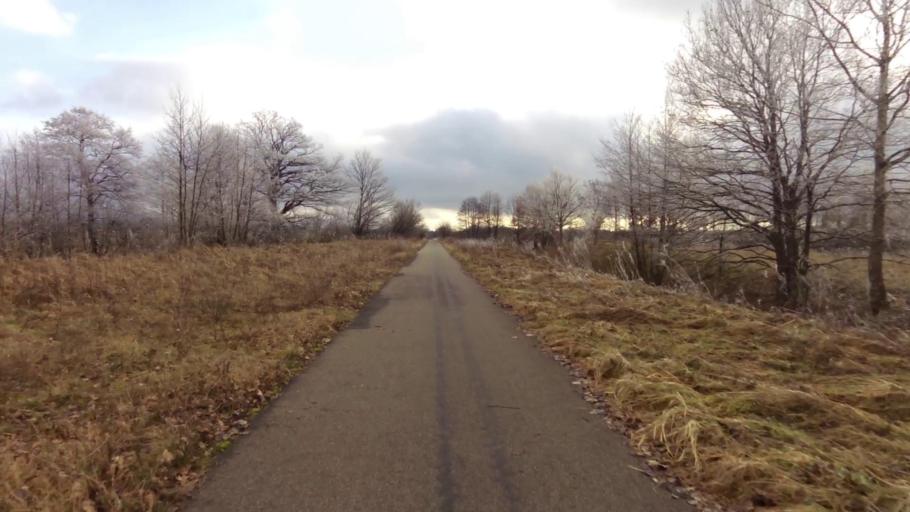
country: PL
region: West Pomeranian Voivodeship
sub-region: Powiat drawski
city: Zlocieniec
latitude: 53.6292
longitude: 16.0562
